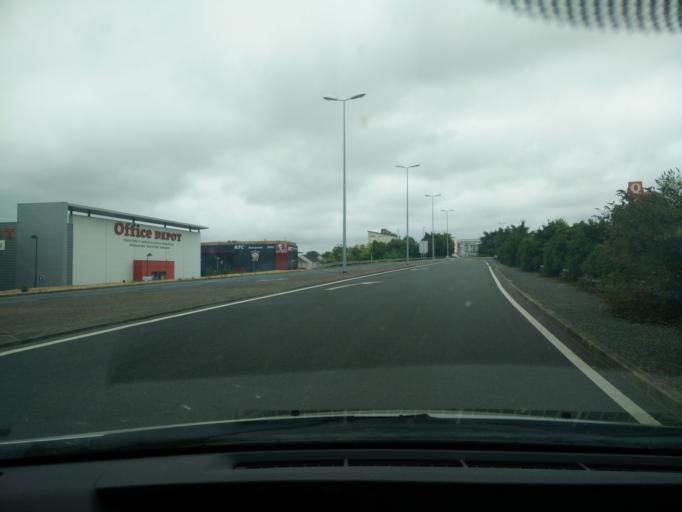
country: FR
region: Pays de la Loire
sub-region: Departement de Maine-et-Loire
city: Angers
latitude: 47.4667
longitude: -0.5259
